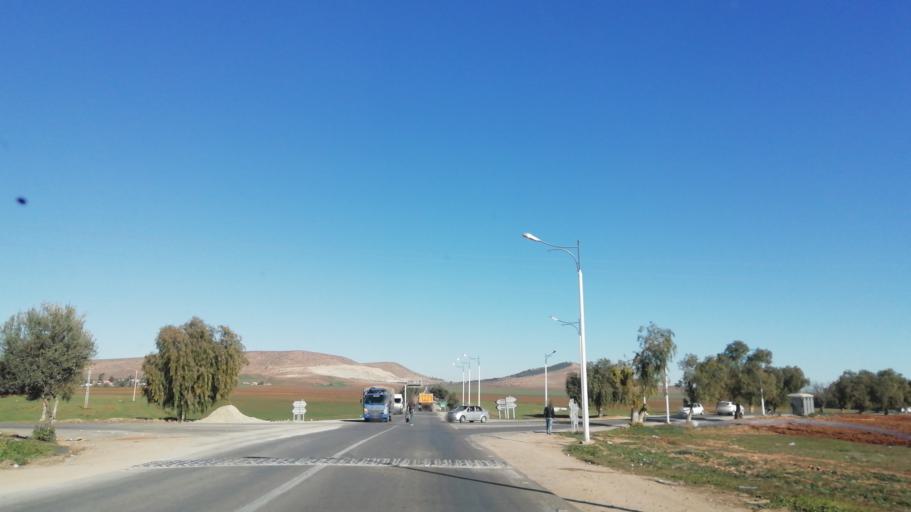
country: DZ
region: Mascara
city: Mascara
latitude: 35.2162
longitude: 0.1121
